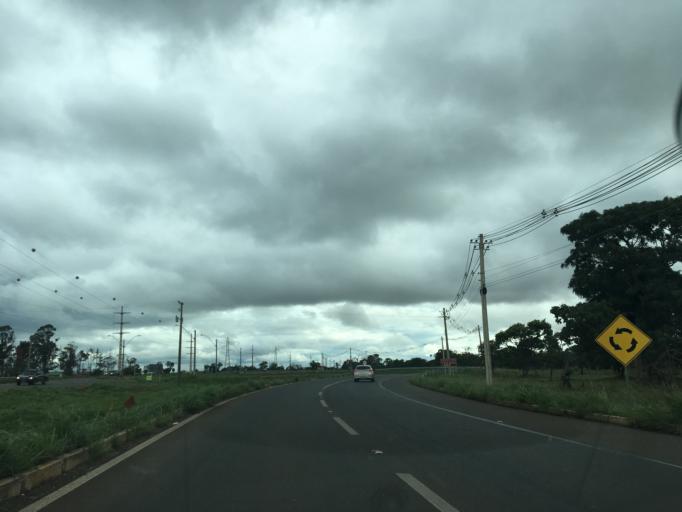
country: BR
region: Federal District
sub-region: Brasilia
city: Brasilia
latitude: -15.8984
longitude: -47.8196
